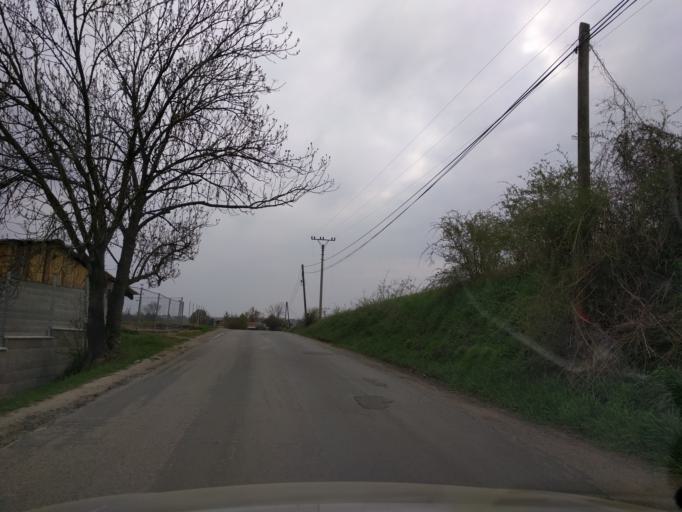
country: CZ
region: Central Bohemia
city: Cesky Brod
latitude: 50.0628
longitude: 14.8476
